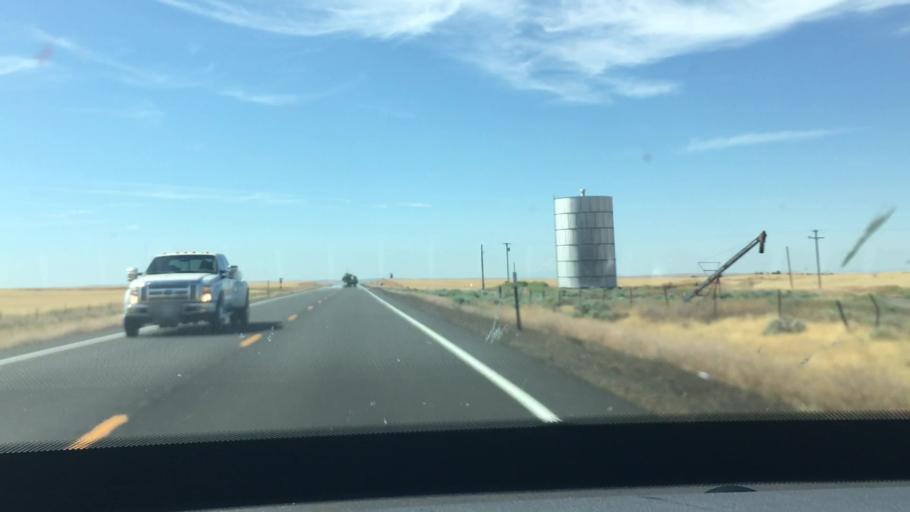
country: US
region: Oregon
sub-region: Sherman County
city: Moro
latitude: 45.3000
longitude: -120.7610
